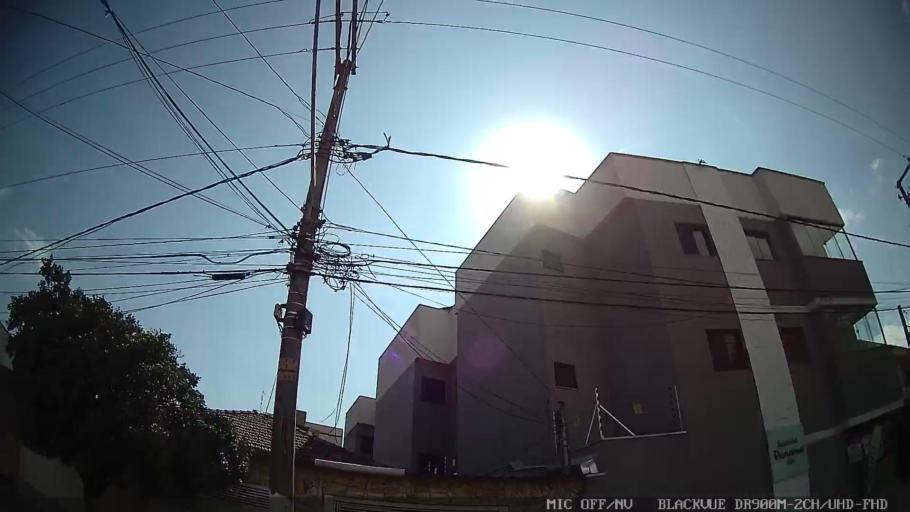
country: BR
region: Sao Paulo
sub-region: Guarulhos
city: Guarulhos
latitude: -23.4931
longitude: -46.4562
